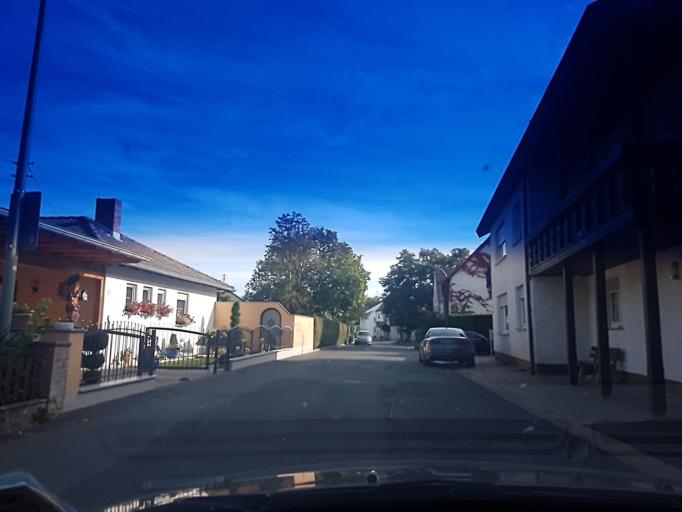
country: DE
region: Bavaria
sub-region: Regierungsbezirk Mittelfranken
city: Burghaslach
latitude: 49.7749
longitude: 10.5604
